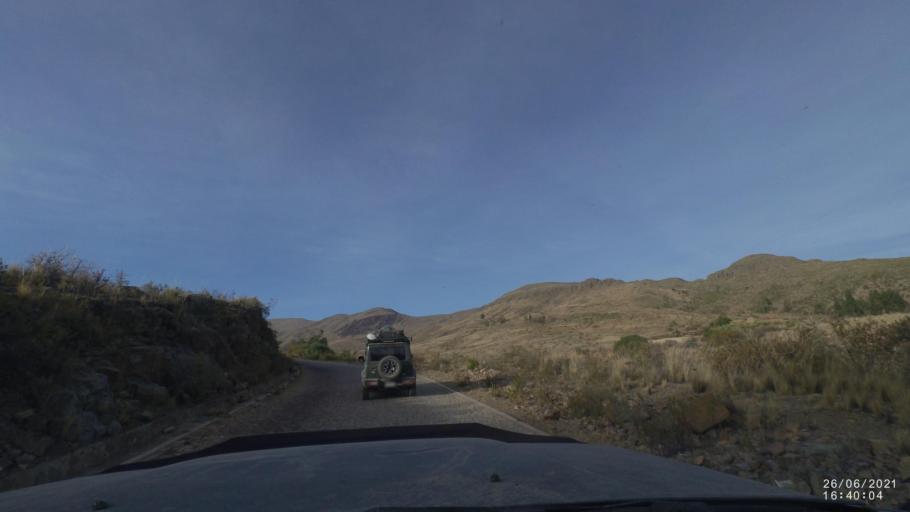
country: BO
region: Cochabamba
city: Arani
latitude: -17.7736
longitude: -65.8137
